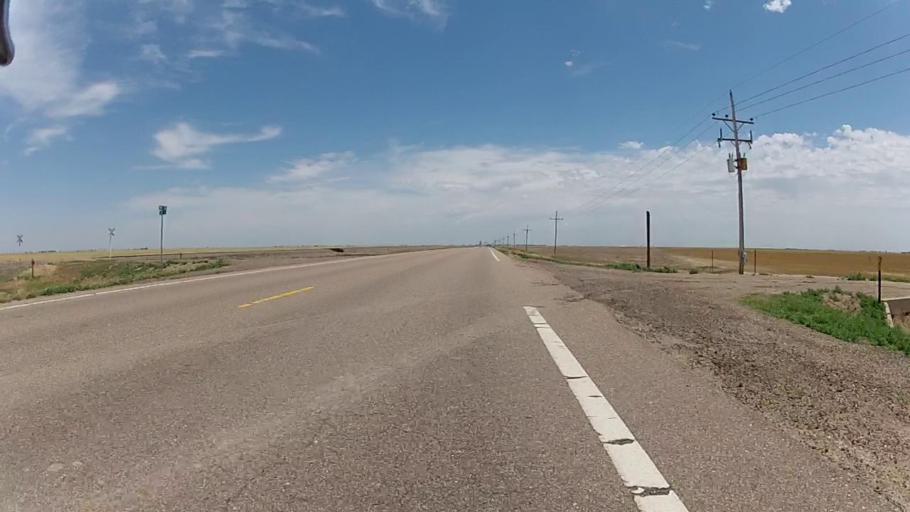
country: US
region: Kansas
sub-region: Haskell County
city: Satanta
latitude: 37.4605
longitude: -100.9258
